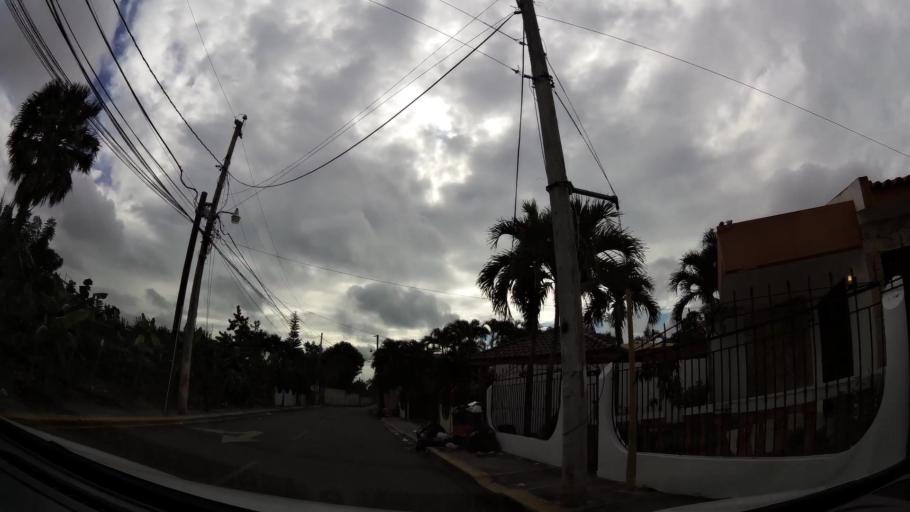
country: DO
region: Santiago
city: Santiago de los Caballeros
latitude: 19.4669
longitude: -70.6539
